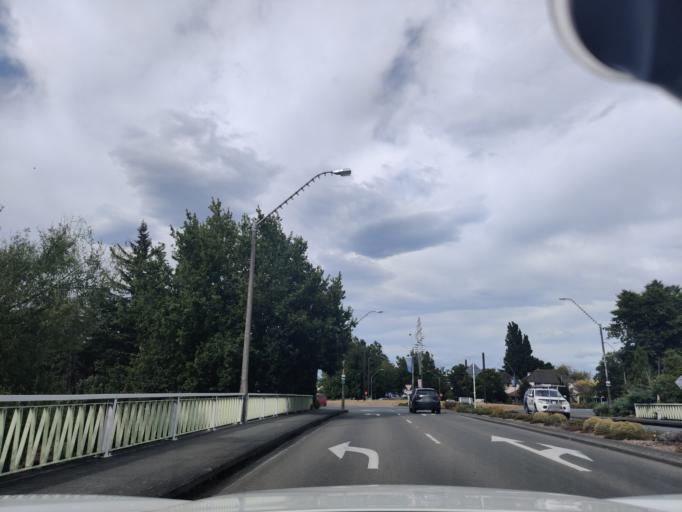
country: NZ
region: Wellington
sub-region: Masterton District
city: Masterton
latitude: -40.9458
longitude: 175.6682
